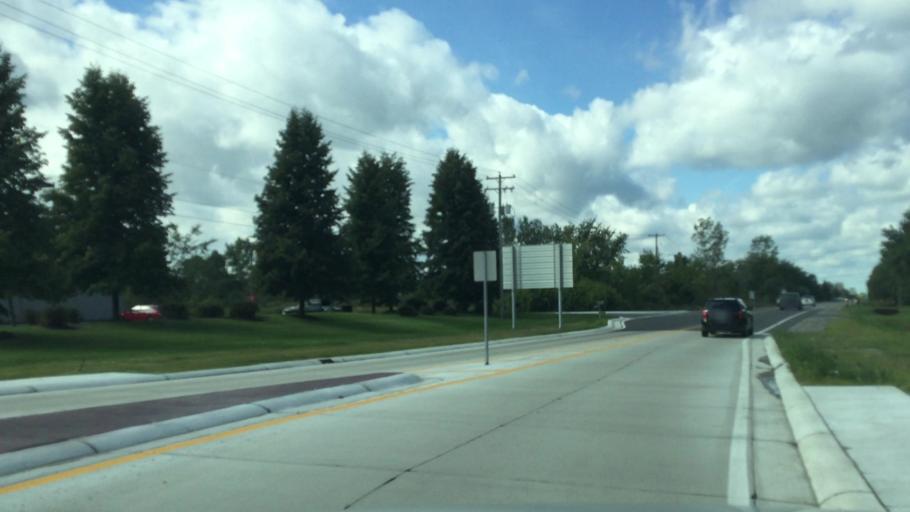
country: US
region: Michigan
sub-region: Genesee County
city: Grand Blanc
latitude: 42.9453
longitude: -83.5986
